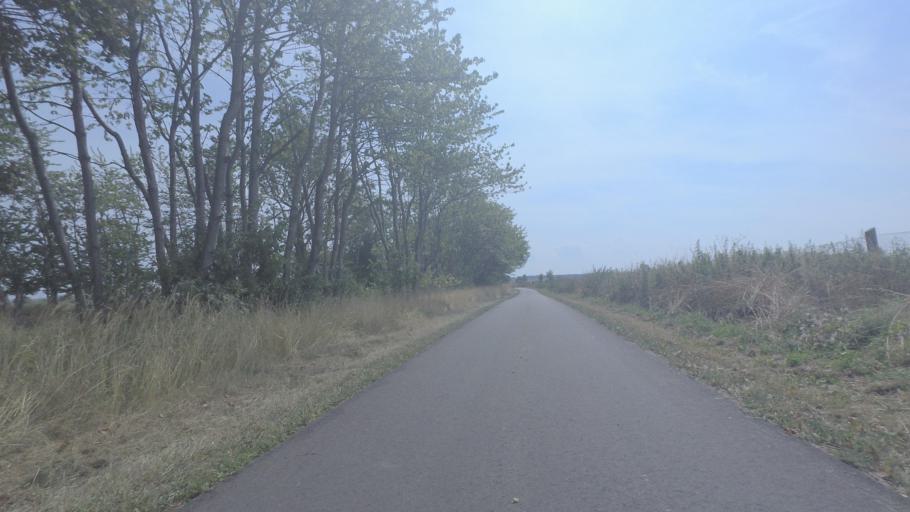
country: DE
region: Mecklenburg-Vorpommern
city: Garz
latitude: 54.2705
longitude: 13.3457
